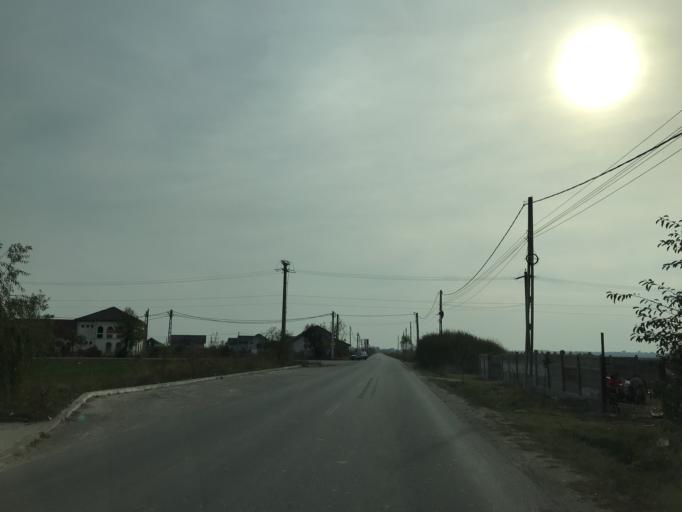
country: RO
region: Olt
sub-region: Comuna Slatioara
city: Slatioara
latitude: 44.3946
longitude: 24.3243
